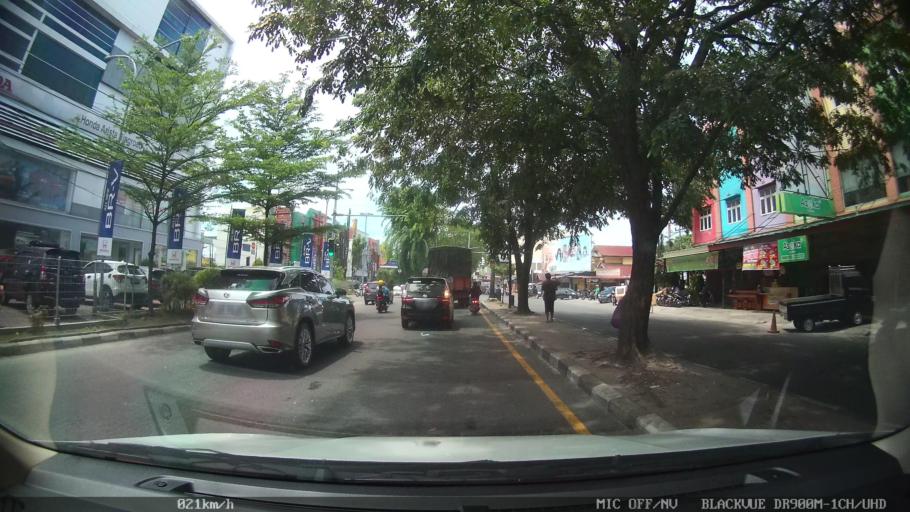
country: ID
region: North Sumatra
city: Sunggal
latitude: 3.5631
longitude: 98.6260
